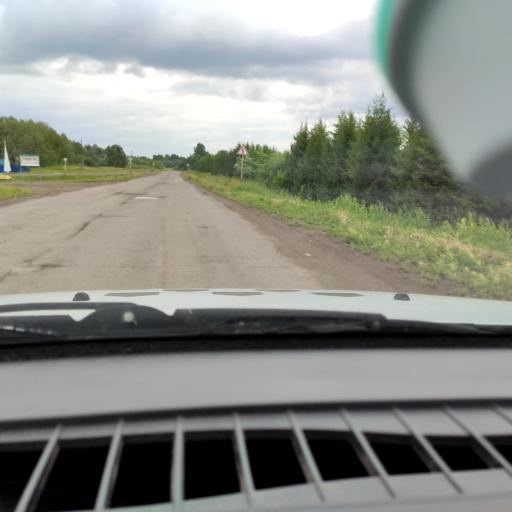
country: RU
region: Perm
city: Uinskoye
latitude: 57.1697
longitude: 56.5643
